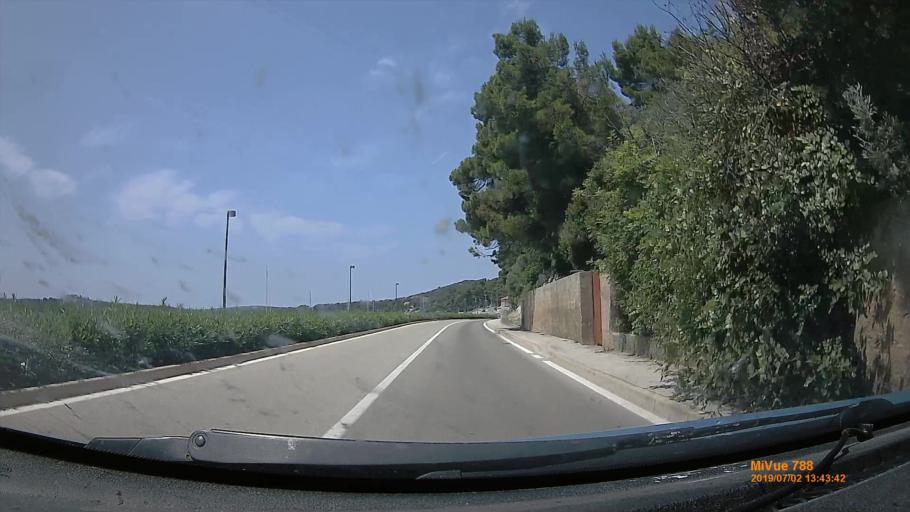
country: HR
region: Primorsko-Goranska
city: Mali Losinj
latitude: 44.5472
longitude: 14.4538
